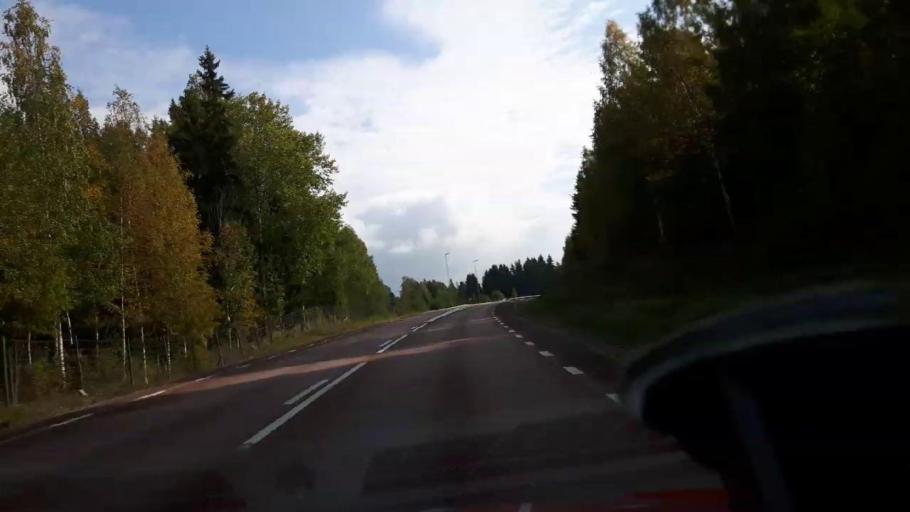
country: SE
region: Gaevleborg
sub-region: Bollnas Kommun
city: Kilafors
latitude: 61.2171
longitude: 16.7281
